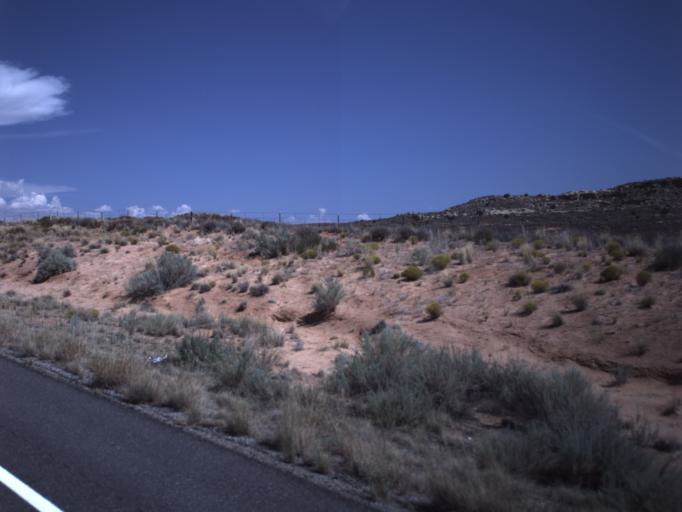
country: US
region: Utah
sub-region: San Juan County
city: Blanding
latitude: 37.3483
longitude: -109.5190
